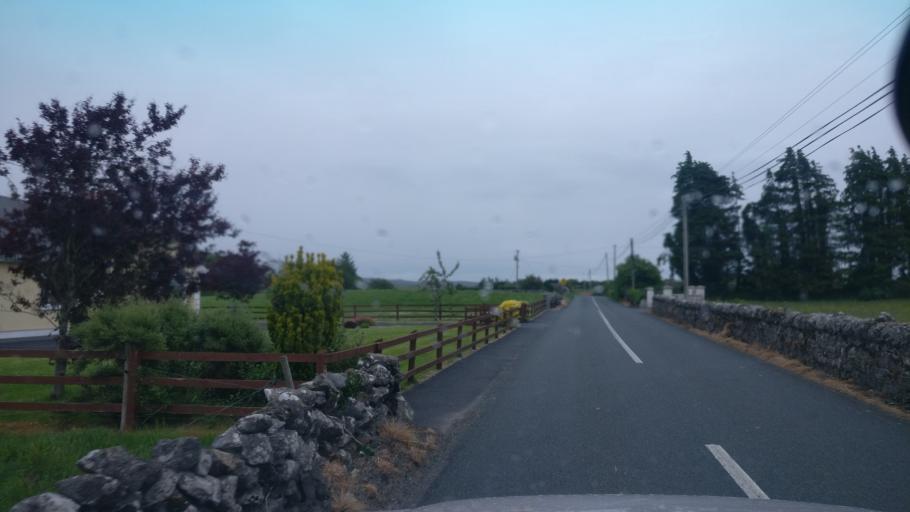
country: IE
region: Connaught
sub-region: County Galway
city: Gort
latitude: 53.0735
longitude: -8.7901
